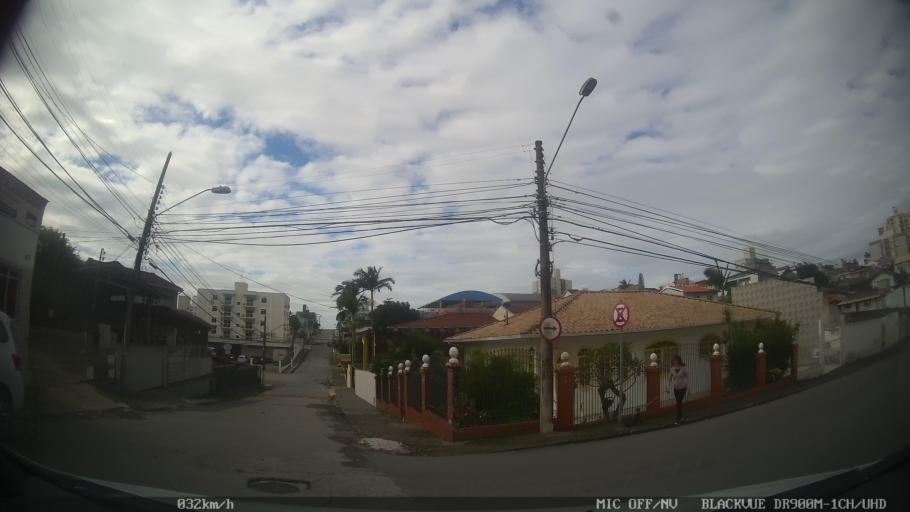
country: BR
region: Santa Catarina
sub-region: Sao Jose
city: Campinas
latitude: -27.5751
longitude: -48.6103
